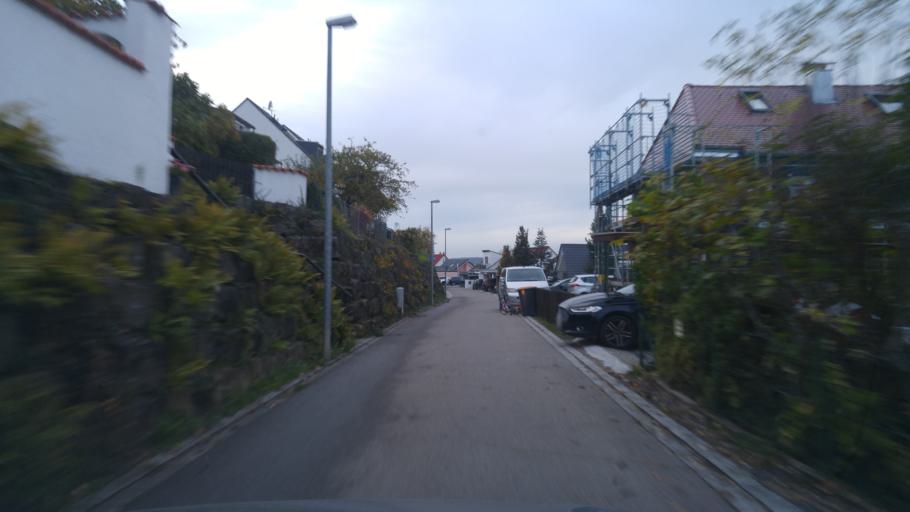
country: DE
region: Baden-Wuerttemberg
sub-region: Regierungsbezirk Stuttgart
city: Leonberg
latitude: 48.8048
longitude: 9.0241
